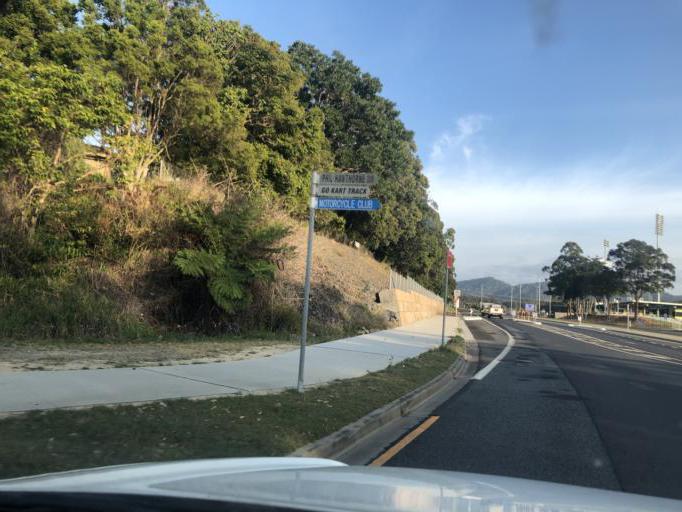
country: AU
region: New South Wales
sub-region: Coffs Harbour
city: Toormina
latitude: -30.3249
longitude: 153.0961
